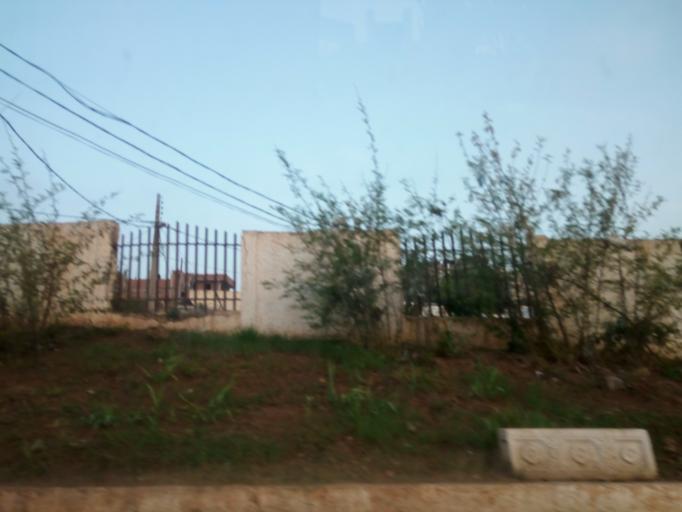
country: DZ
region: Tipaza
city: Bou Ismail
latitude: 36.6049
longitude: 2.6144
